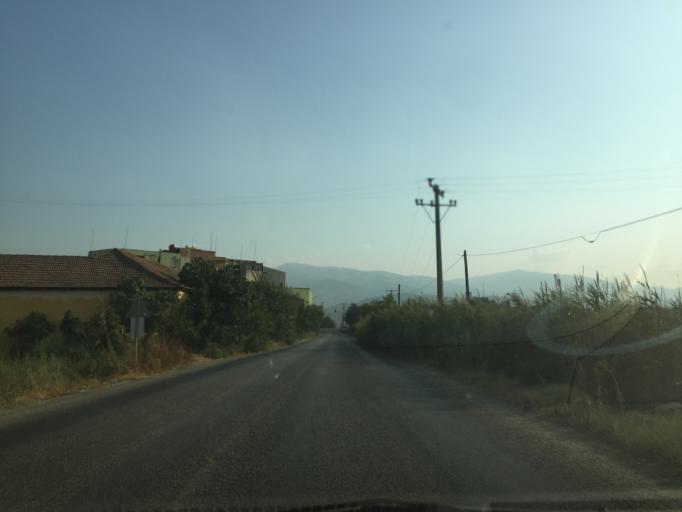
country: TR
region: Manisa
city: Salihli
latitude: 38.4970
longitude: 28.1824
